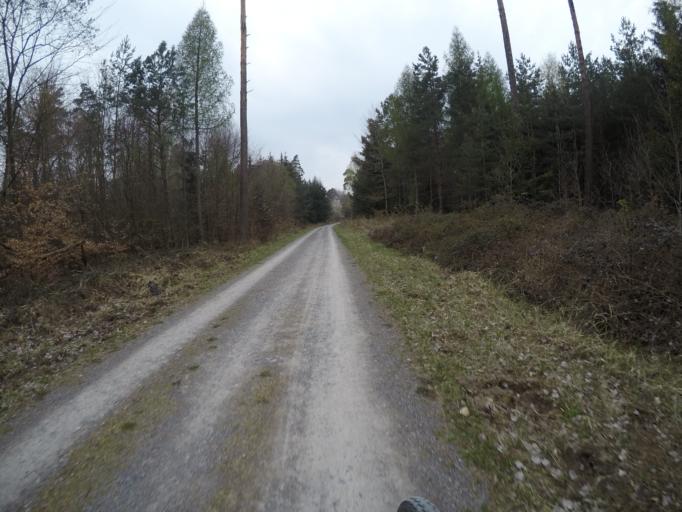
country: DE
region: Baden-Wuerttemberg
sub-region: Regierungsbezirk Stuttgart
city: Schonaich
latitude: 48.7174
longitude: 9.0773
